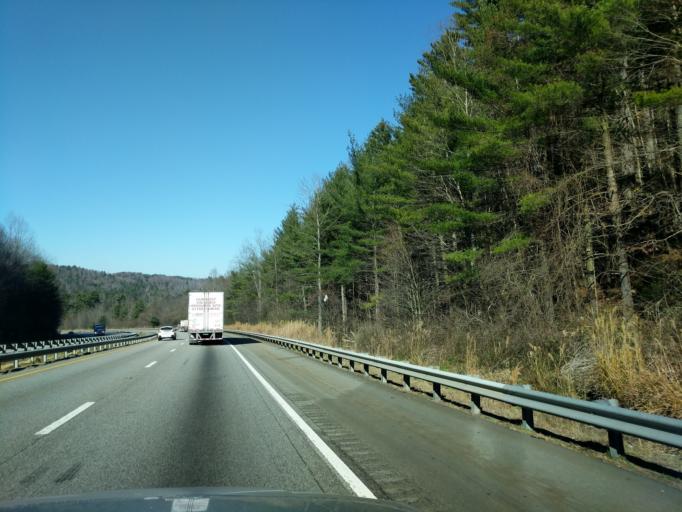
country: US
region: North Carolina
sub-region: Henderson County
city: East Flat Rock
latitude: 35.2683
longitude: -82.3670
